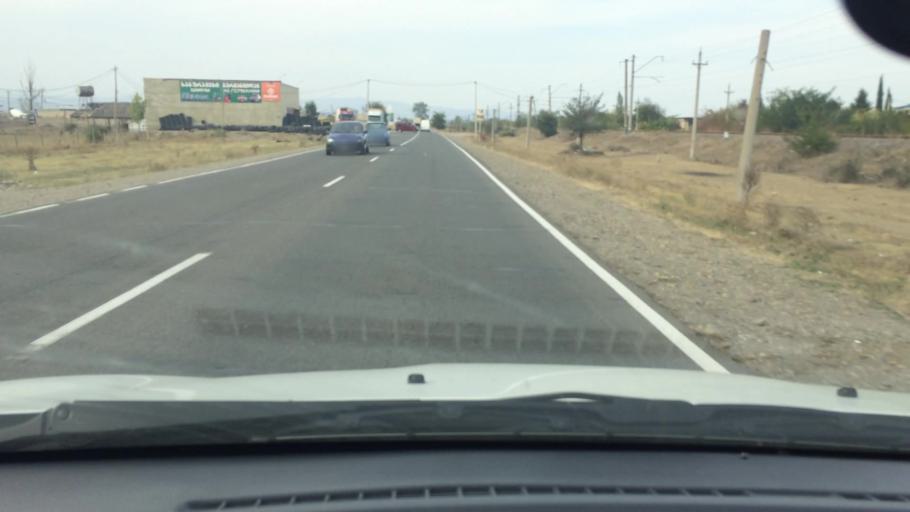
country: GE
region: Kvemo Kartli
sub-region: Marneuli
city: Marneuli
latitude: 41.4356
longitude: 44.8194
